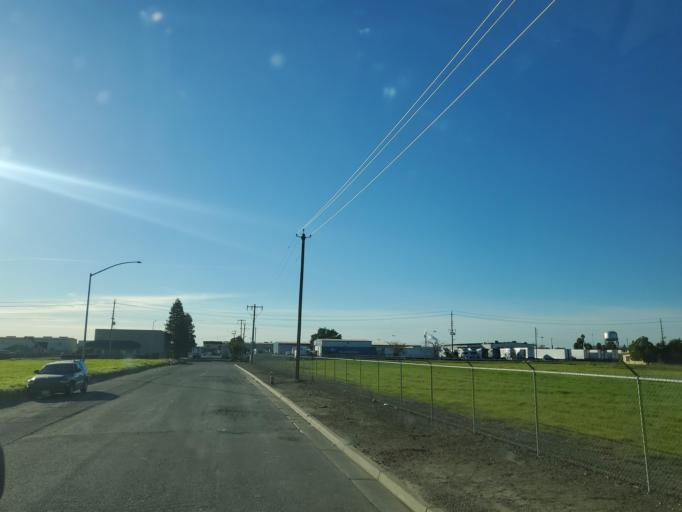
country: US
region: California
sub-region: San Joaquin County
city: Stockton
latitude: 37.9398
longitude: -121.3049
